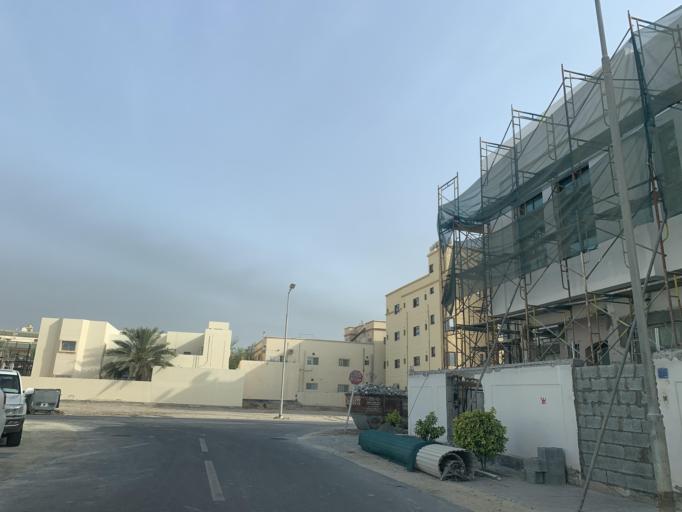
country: BH
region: Northern
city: Madinat `Isa
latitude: 26.1911
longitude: 50.5586
